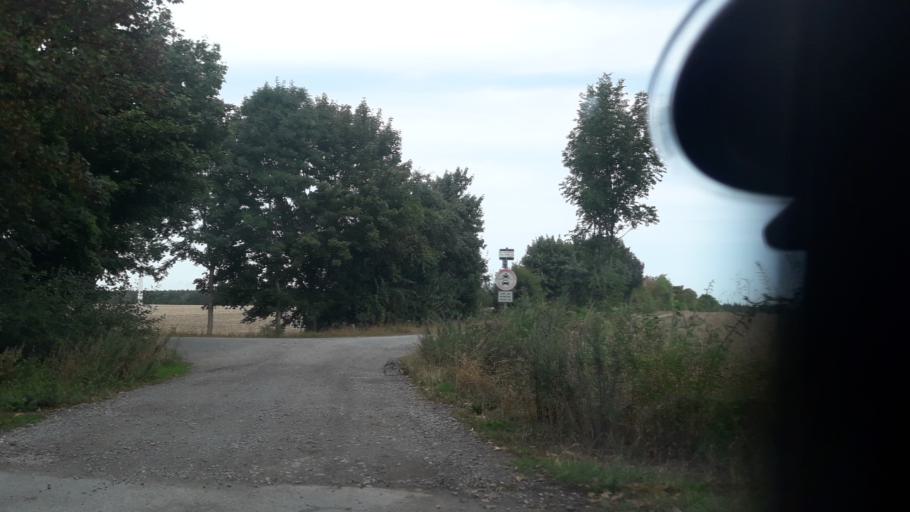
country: DE
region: Lower Saxony
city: Gross Twulpstedt
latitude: 52.3654
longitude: 10.8825
